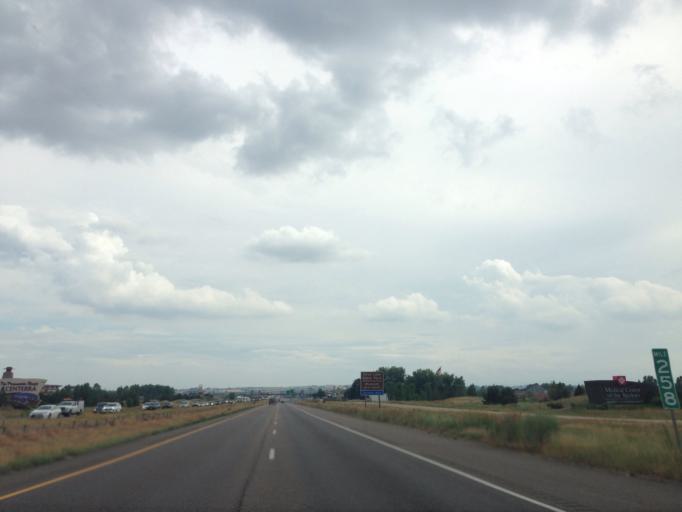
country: US
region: Colorado
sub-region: Larimer County
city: Loveland
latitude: 40.4173
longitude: -104.9928
